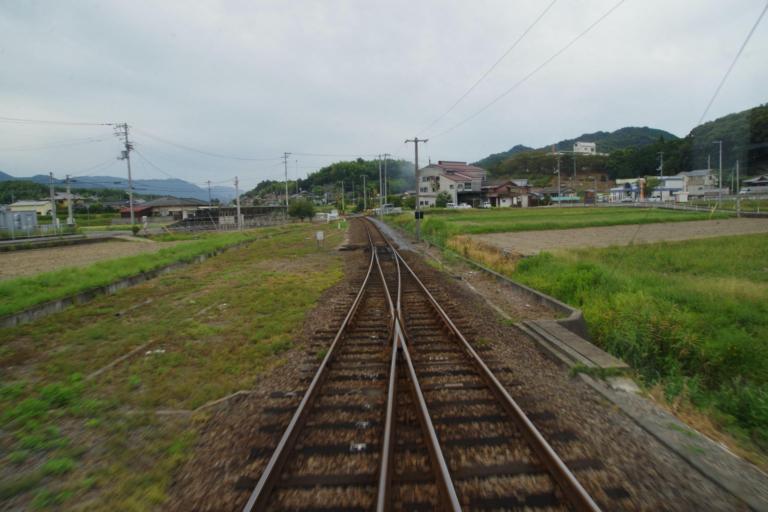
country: JP
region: Tokushima
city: Ikedacho
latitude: 34.1552
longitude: 133.8484
